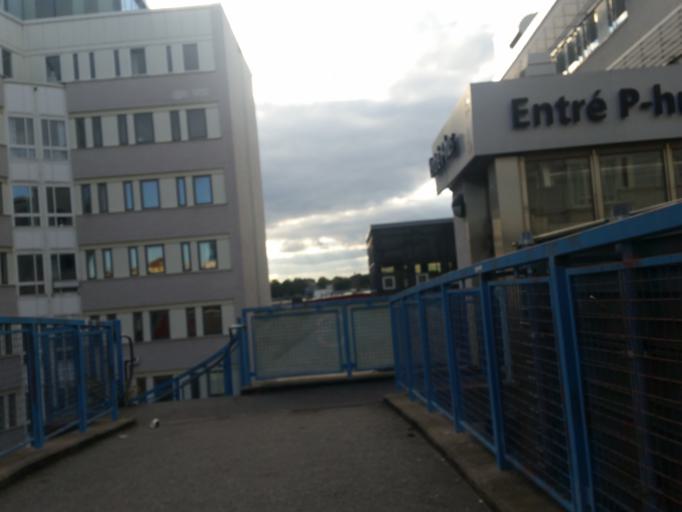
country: SE
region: Stockholm
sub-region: Stockholms Kommun
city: Arsta
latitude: 59.2920
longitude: 18.0820
